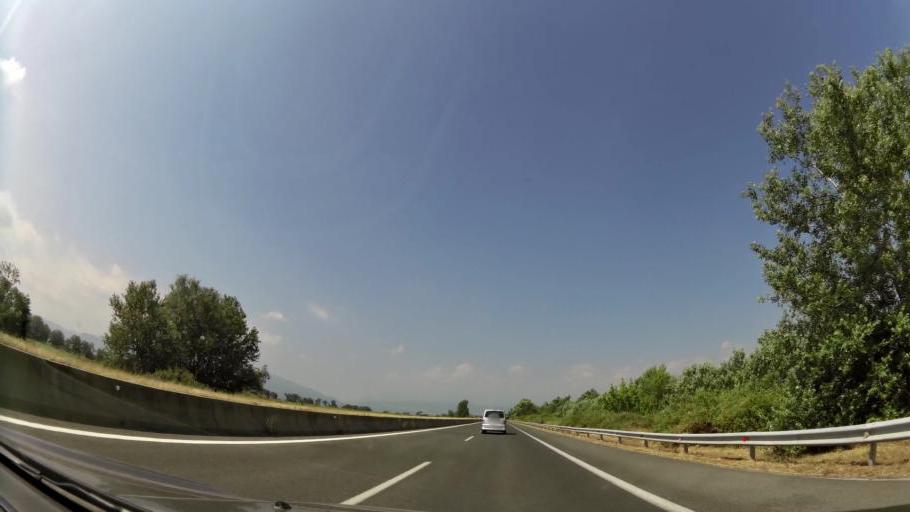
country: GR
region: Central Macedonia
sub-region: Nomos Imathias
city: Kouloura
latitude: 40.5530
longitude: 22.3414
